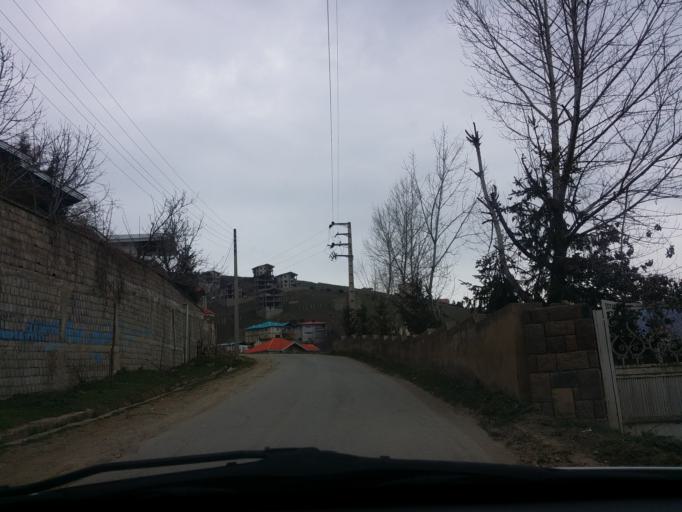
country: IR
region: Mazandaran
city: `Abbasabad
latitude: 36.5334
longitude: 51.1613
